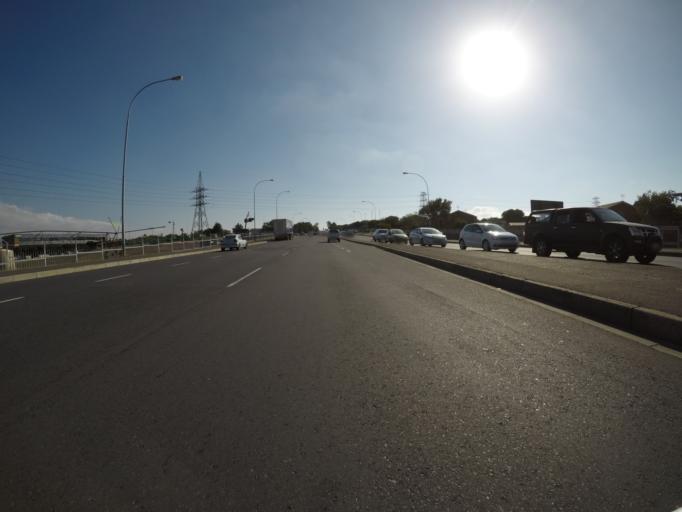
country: ZA
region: Western Cape
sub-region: City of Cape Town
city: Kraaifontein
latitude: -33.8873
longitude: 18.6732
